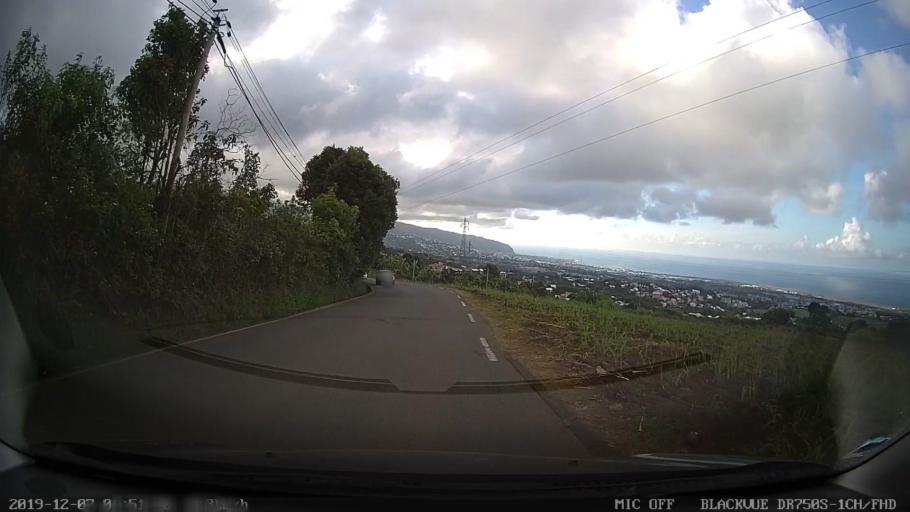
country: RE
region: Reunion
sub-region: Reunion
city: Sainte-Marie
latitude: -20.9415
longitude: 55.5348
